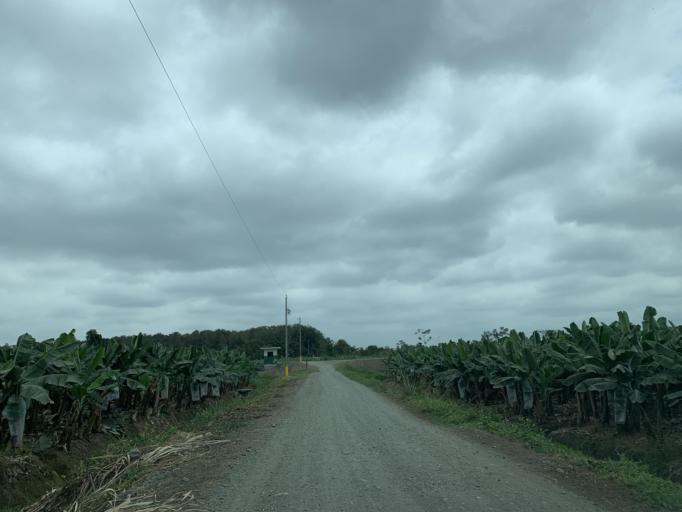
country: EC
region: Guayas
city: Coronel Marcelino Mariduena
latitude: -2.3306
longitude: -79.4543
